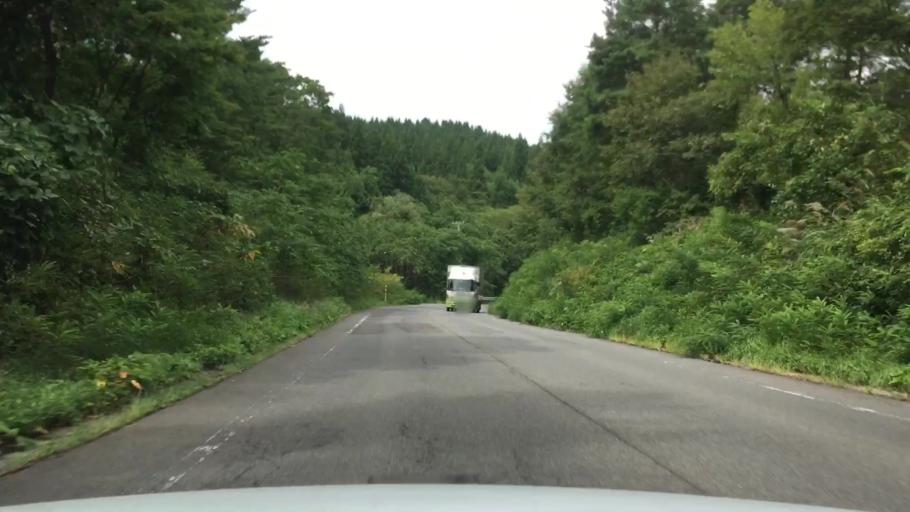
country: JP
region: Aomori
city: Shimokizukuri
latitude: 40.7250
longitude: 140.2556
